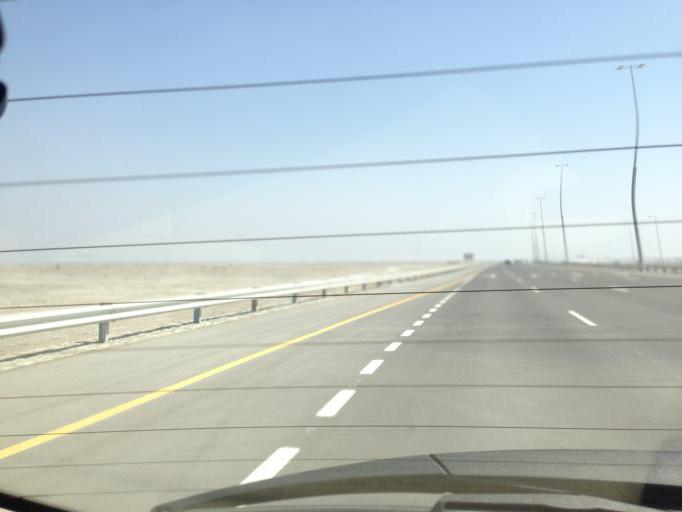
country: OM
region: Al Batinah
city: Barka'
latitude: 23.5600
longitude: 57.6958
